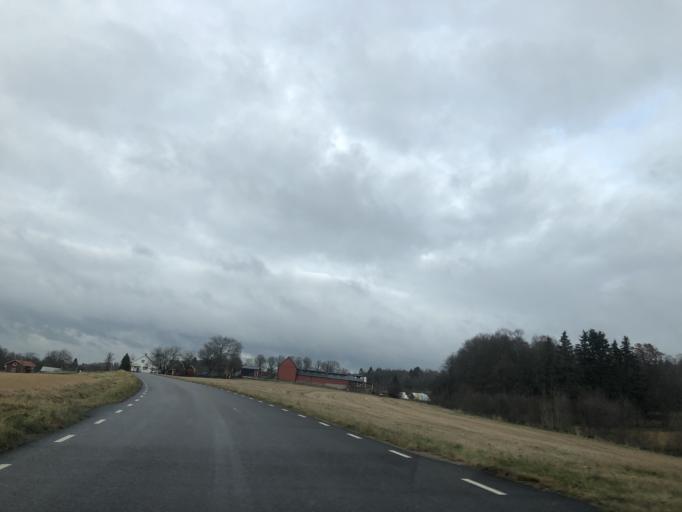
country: SE
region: Vaestra Goetaland
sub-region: Ulricehamns Kommun
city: Ulricehamn
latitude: 57.8138
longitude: 13.2436
